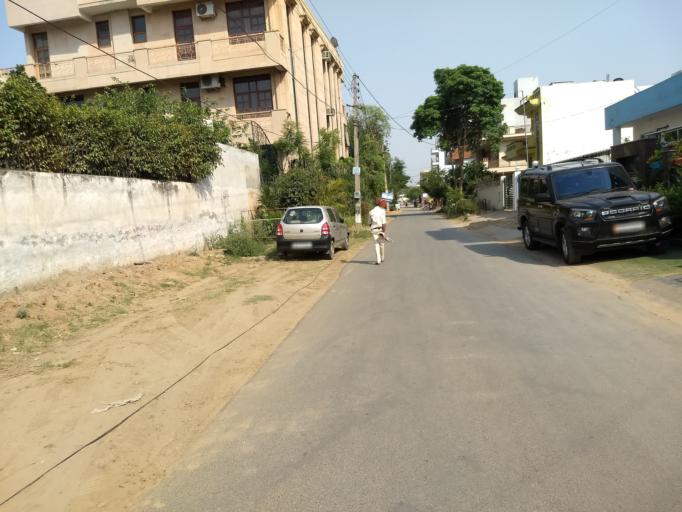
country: IN
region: Haryana
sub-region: Gurgaon
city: Gurgaon
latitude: 28.4373
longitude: 77.0469
